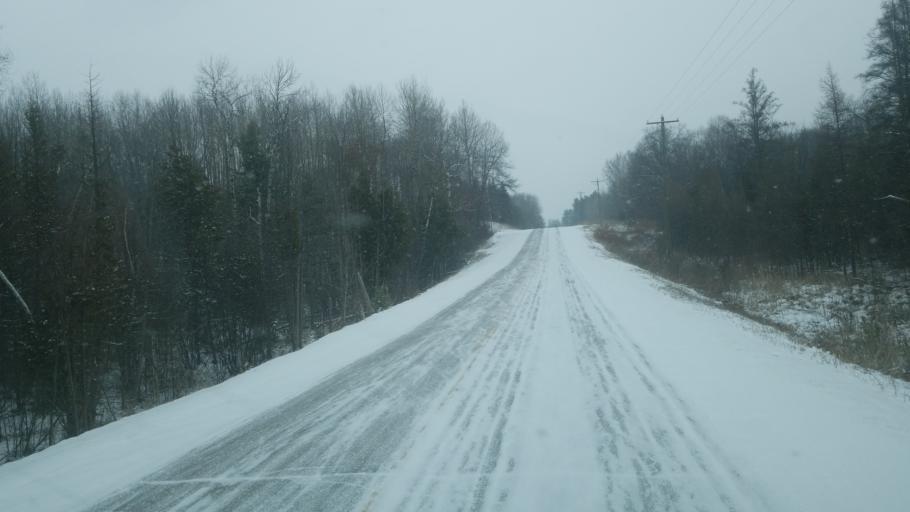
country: US
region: Michigan
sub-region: Osceola County
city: Reed City
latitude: 43.8022
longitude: -85.4024
